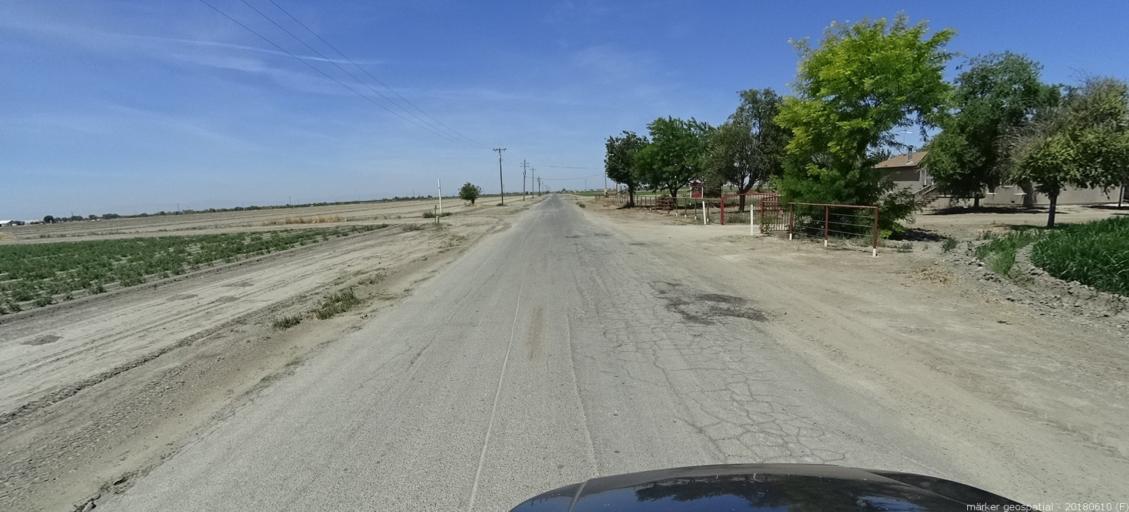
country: US
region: California
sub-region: Merced County
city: Dos Palos
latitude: 37.0546
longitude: -120.5145
